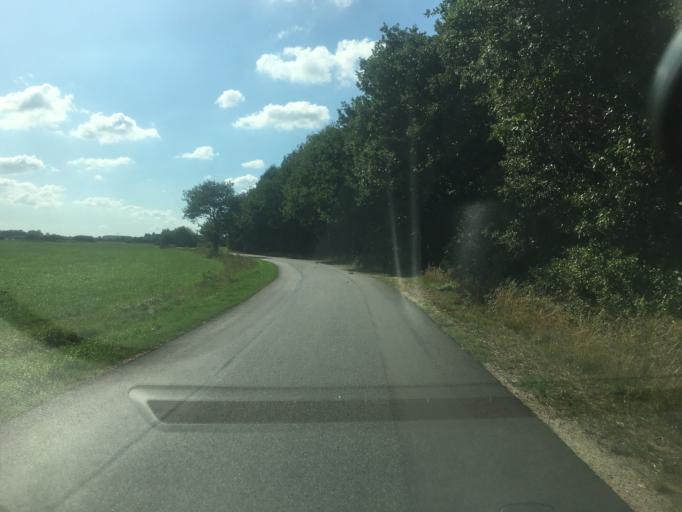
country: DK
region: South Denmark
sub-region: Tonder Kommune
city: Logumkloster
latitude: 54.9928
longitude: 9.0063
